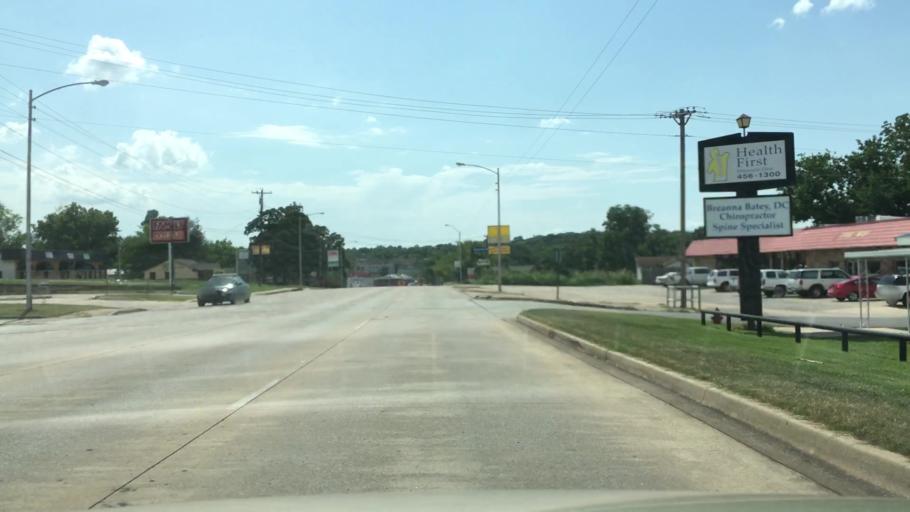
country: US
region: Oklahoma
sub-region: Cherokee County
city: Tahlequah
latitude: 35.9154
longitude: -94.9643
